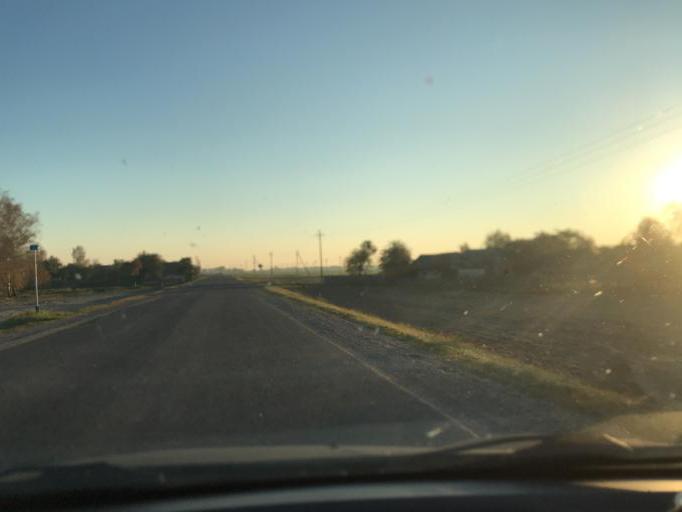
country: BY
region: Gomel
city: Brahin
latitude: 51.7941
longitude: 30.2609
